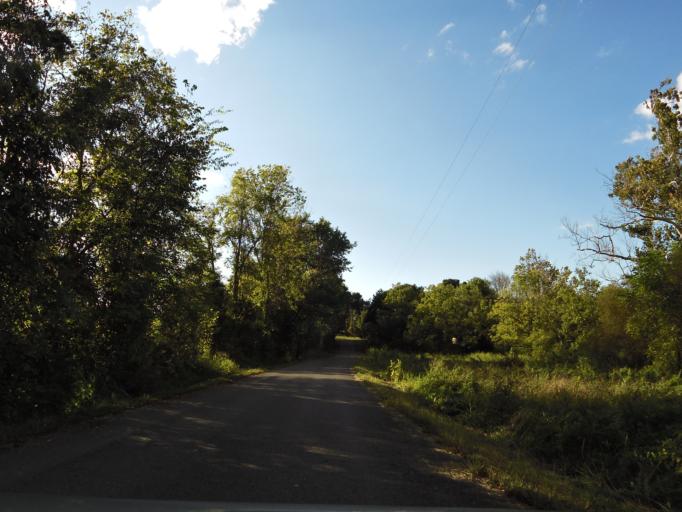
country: US
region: Tennessee
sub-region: Grainger County
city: Blaine
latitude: 36.1430
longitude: -83.7360
